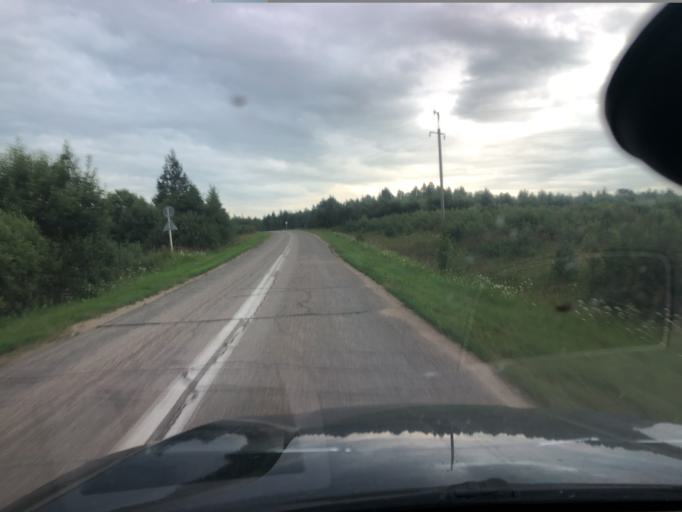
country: RU
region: Jaroslavl
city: Pereslavl'-Zalesskiy
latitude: 57.0137
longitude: 38.9616
